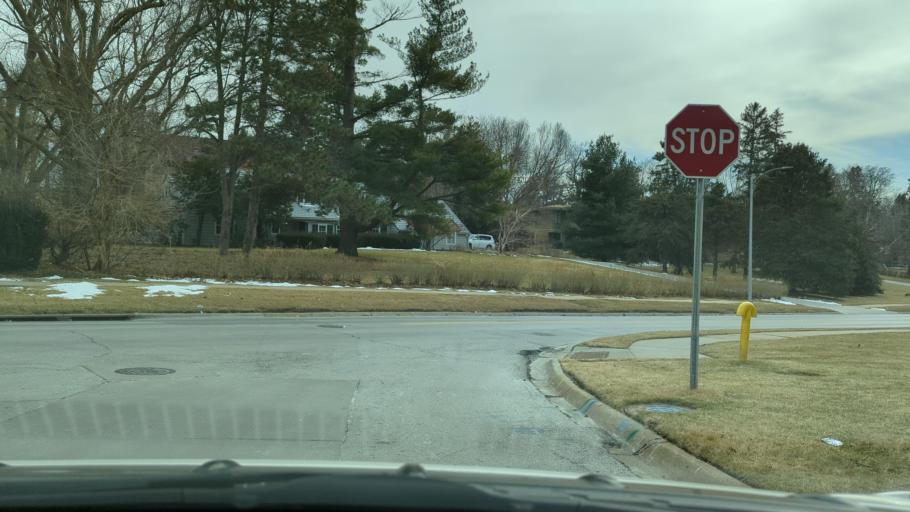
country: US
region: Nebraska
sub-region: Douglas County
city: Ralston
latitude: 41.2649
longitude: -96.0143
